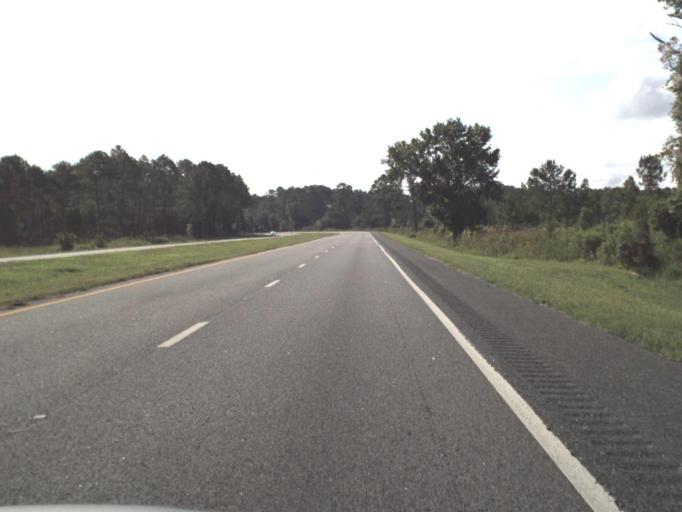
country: US
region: Florida
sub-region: Alachua County
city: Gainesville
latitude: 29.5168
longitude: -82.2953
